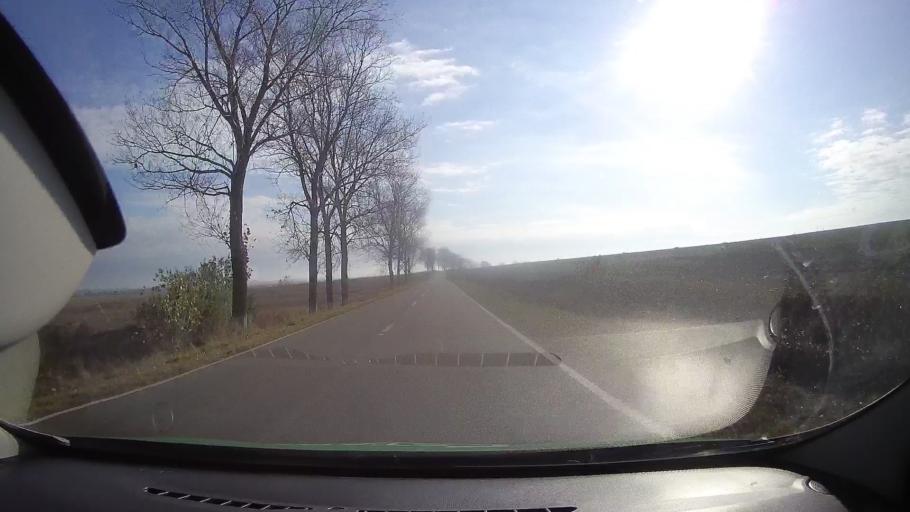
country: RO
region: Tulcea
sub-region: Comuna Mahmudia
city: Mahmudia
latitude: 45.0683
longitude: 29.1021
